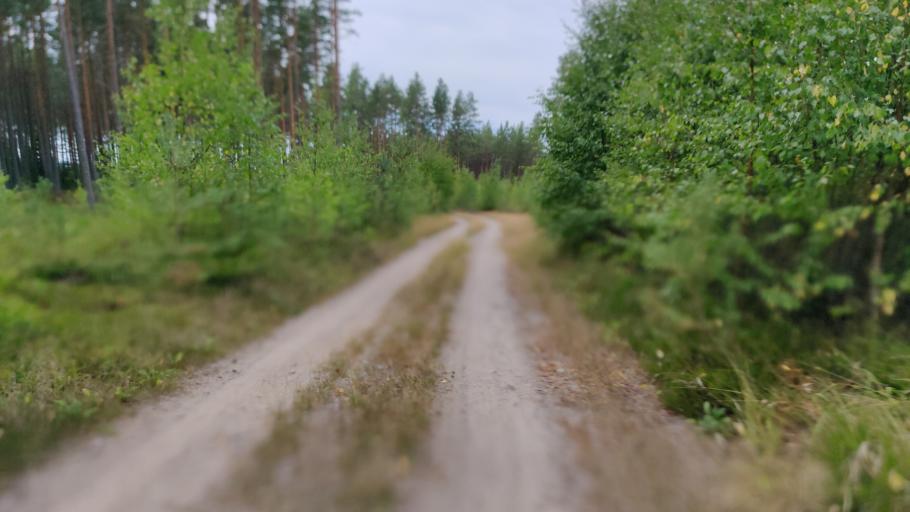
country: SE
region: Vaermland
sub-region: Hagfors Kommun
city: Hagfors
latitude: 60.0350
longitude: 13.5413
